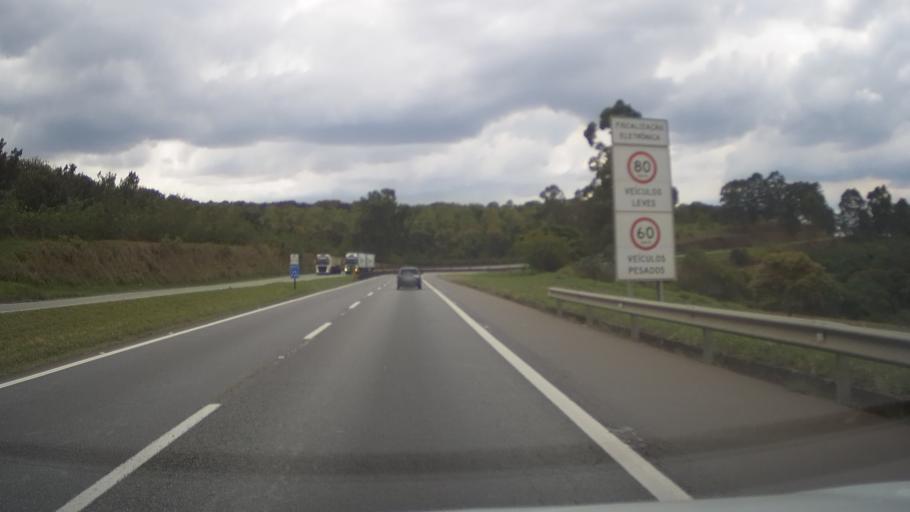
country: BR
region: Minas Gerais
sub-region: Tres Coracoes
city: Tres Coracoes
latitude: -21.5036
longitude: -45.2150
